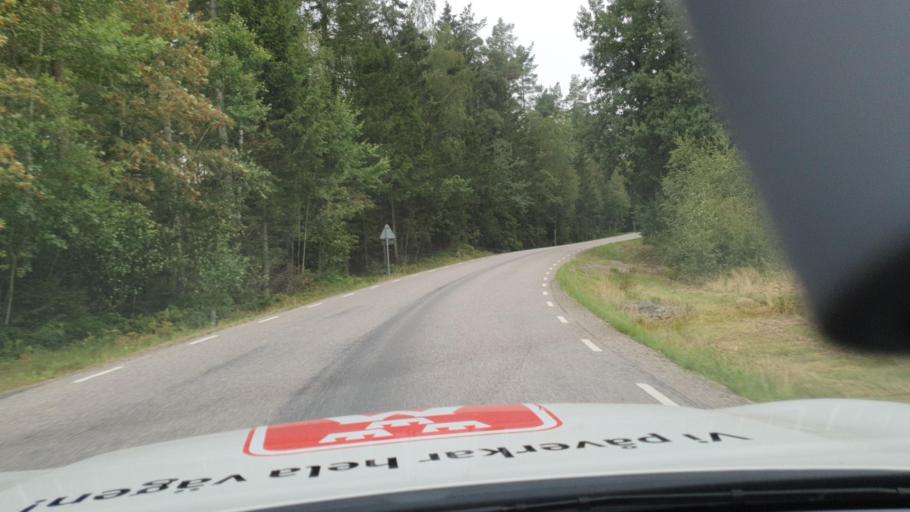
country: SE
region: Vaestra Goetaland
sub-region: Vanersborgs Kommun
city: Vanersborg
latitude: 58.4917
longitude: 12.2143
